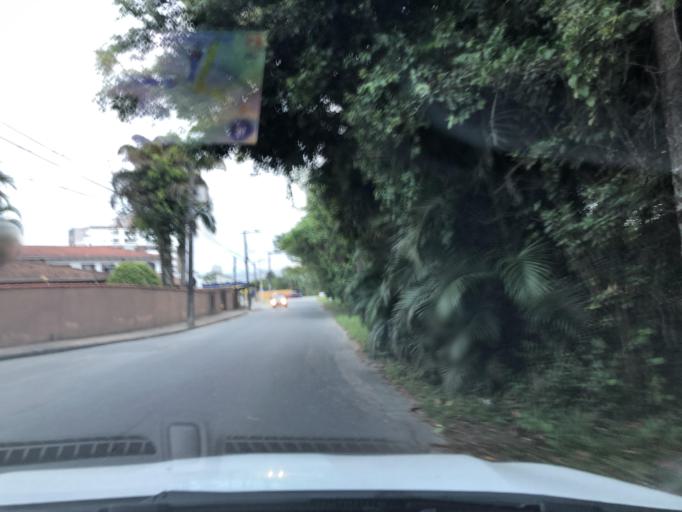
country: BR
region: Santa Catarina
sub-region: Joinville
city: Joinville
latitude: -26.2728
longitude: -48.8706
